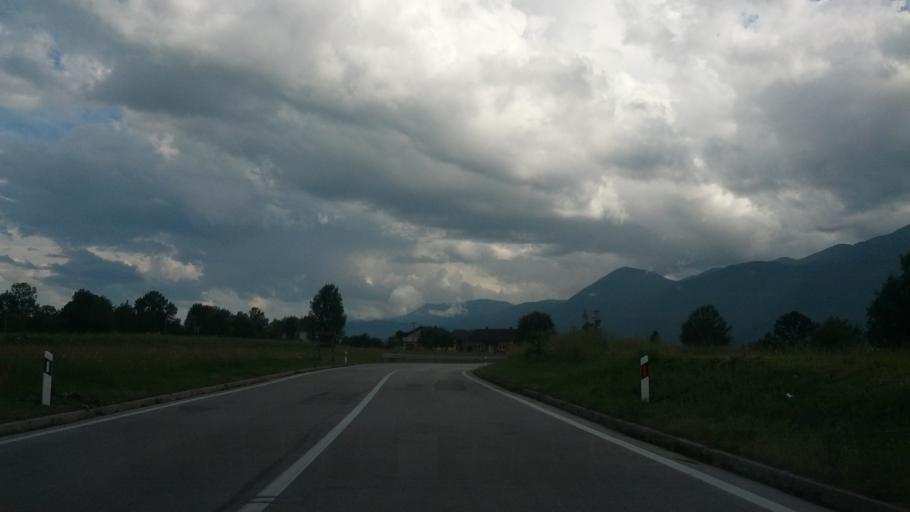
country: BA
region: Federation of Bosnia and Herzegovina
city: Izacic
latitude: 44.8763
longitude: 15.7688
